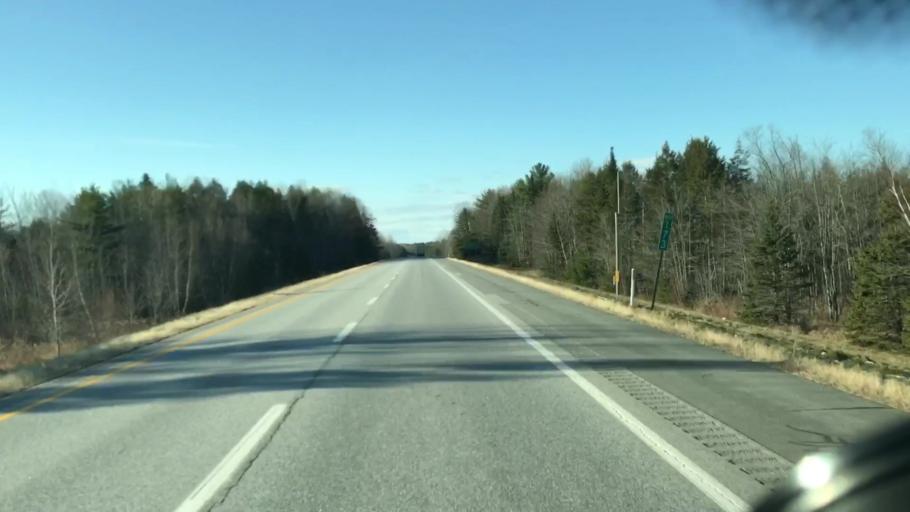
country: US
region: Maine
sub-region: Penobscot County
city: Carmel
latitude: 44.7643
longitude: -68.9886
